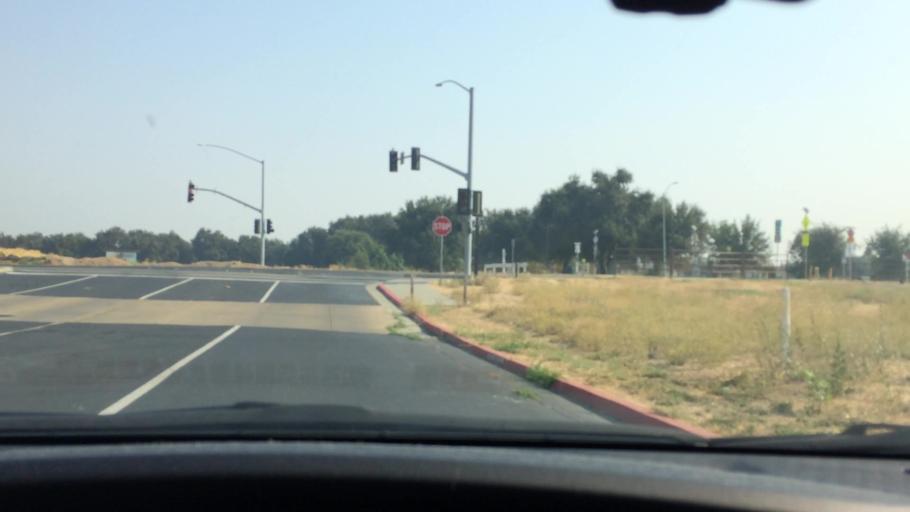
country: US
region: California
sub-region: Yolo County
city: West Sacramento
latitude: 38.5509
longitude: -121.5344
